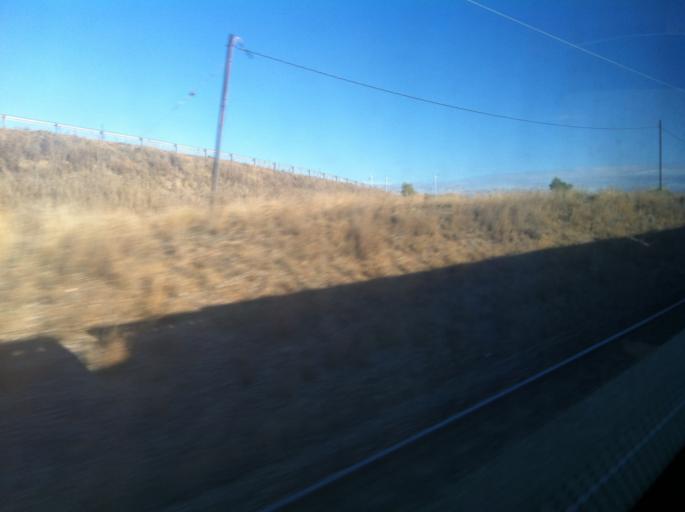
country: ES
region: Castille and Leon
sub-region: Provincia de Burgos
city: Villazopeque
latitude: 42.1876
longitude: -4.0356
